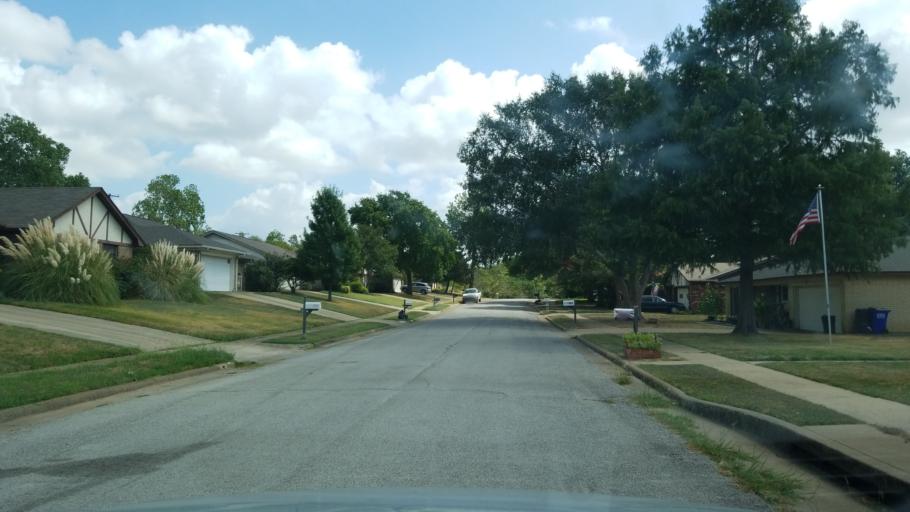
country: US
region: Texas
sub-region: Tarrant County
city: Euless
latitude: 32.8477
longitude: -97.0982
